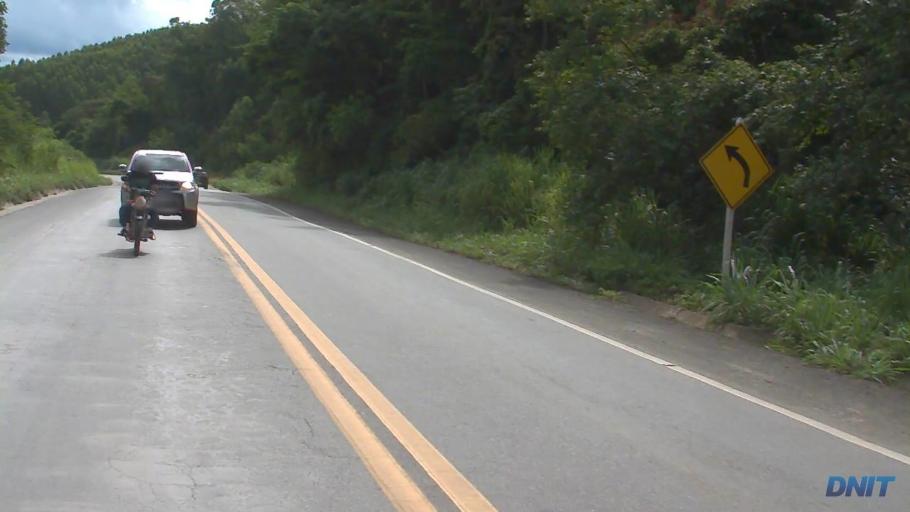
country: BR
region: Minas Gerais
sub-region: Ipaba
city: Ipaba
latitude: -19.3337
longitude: -42.4238
